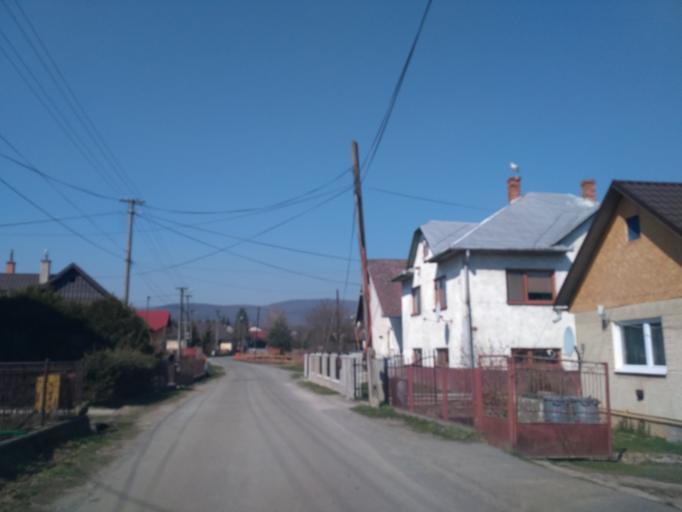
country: SK
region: Presovsky
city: Vranov nad Topl'ou
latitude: 48.8241
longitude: 21.6369
